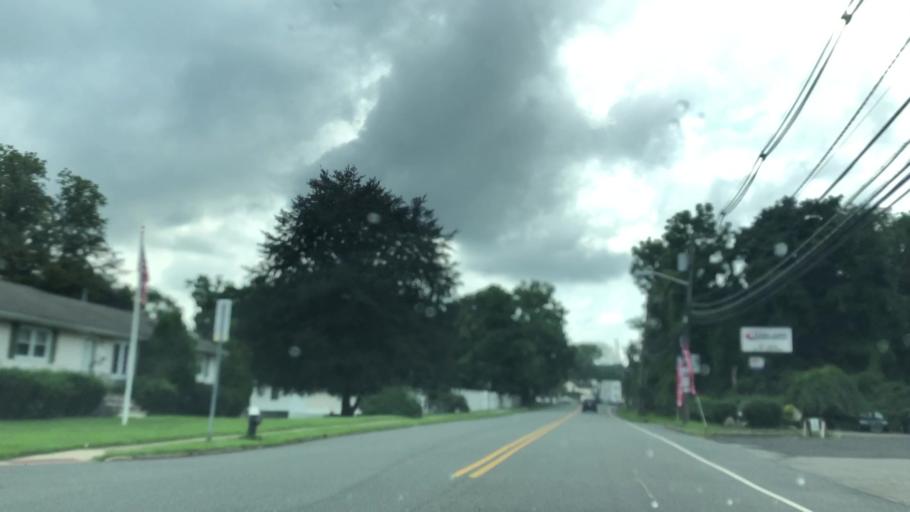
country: US
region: New Jersey
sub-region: Passaic County
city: Singac
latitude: 40.8843
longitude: -74.2236
